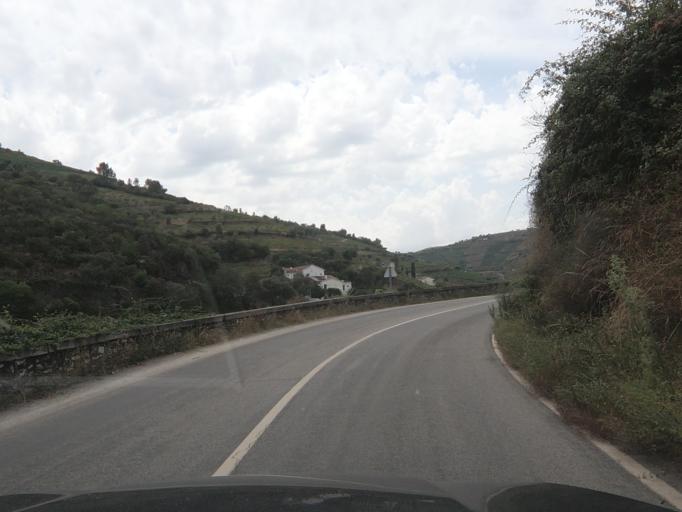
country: PT
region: Vila Real
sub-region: Santa Marta de Penaguiao
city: Santa Marta de Penaguiao
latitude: 41.2248
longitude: -7.7708
